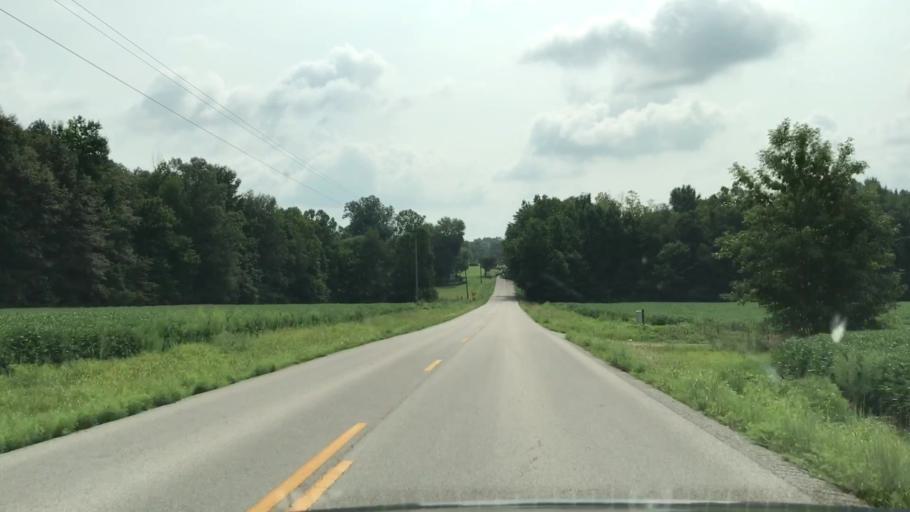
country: US
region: Kentucky
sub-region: Edmonson County
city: Brownsville
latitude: 37.1428
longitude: -86.1884
